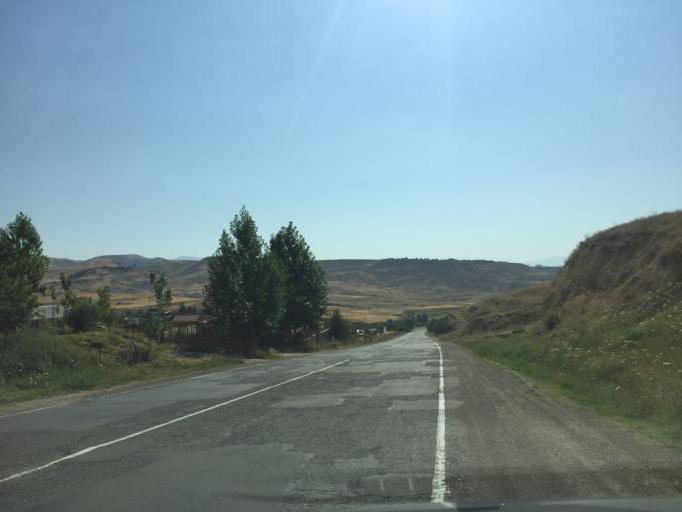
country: AM
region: Vayots' Dzori Marz
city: Rrind
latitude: 39.7620
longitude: 45.1393
